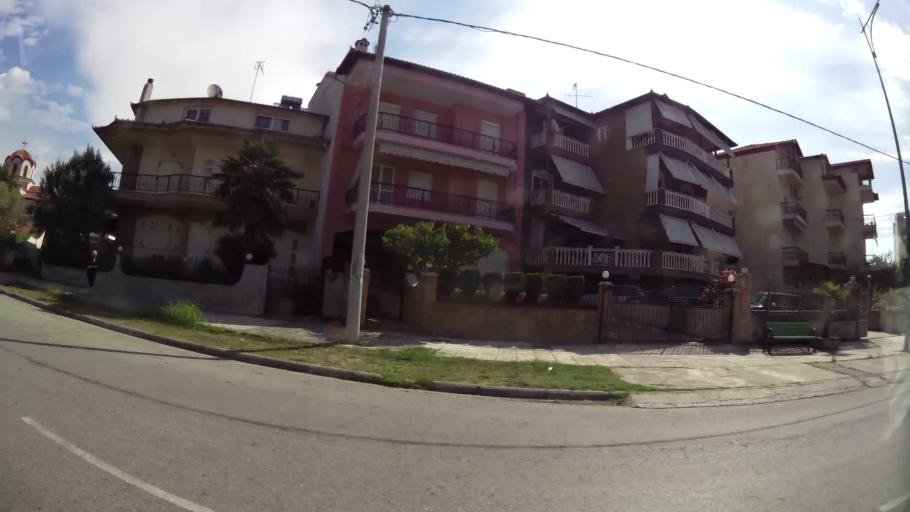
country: GR
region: Central Macedonia
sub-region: Nomos Pierias
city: Katerini
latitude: 40.2808
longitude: 22.5051
